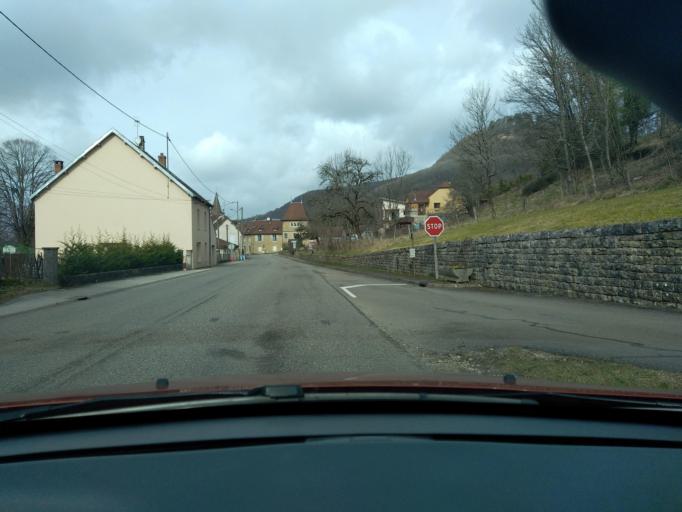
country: FR
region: Franche-Comte
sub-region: Departement du Jura
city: Perrigny
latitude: 46.6518
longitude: 5.6007
